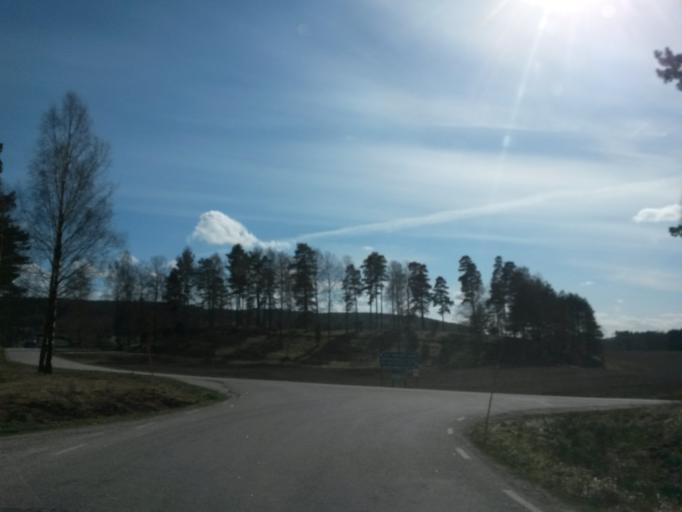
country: SE
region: Vaestra Goetaland
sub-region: Vargarda Kommun
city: Jonstorp
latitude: 57.9889
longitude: 12.7695
